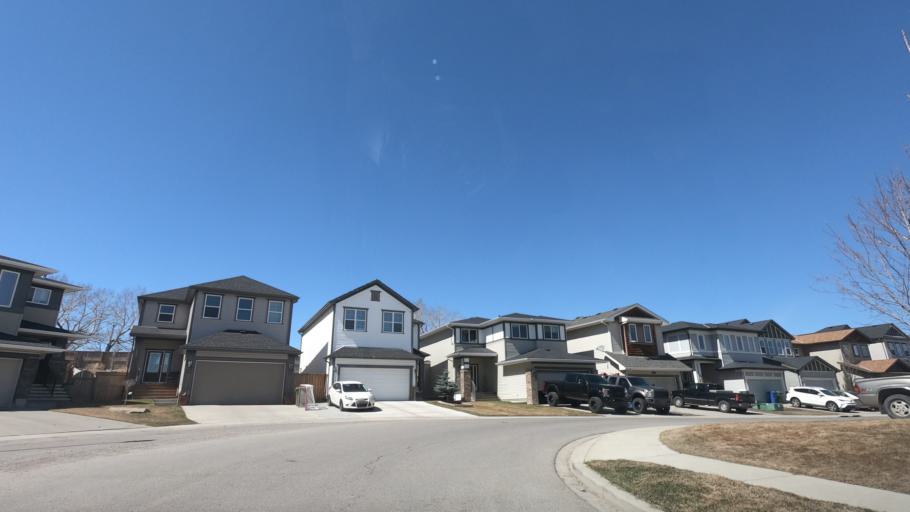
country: CA
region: Alberta
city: Airdrie
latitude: 51.3057
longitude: -114.0475
